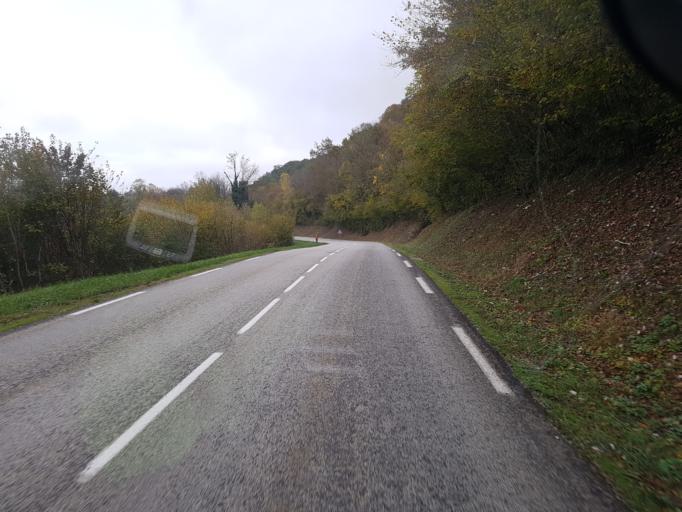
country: FR
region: Rhone-Alpes
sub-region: Departement de la Savoie
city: Yenne
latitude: 45.6518
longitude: 5.6988
